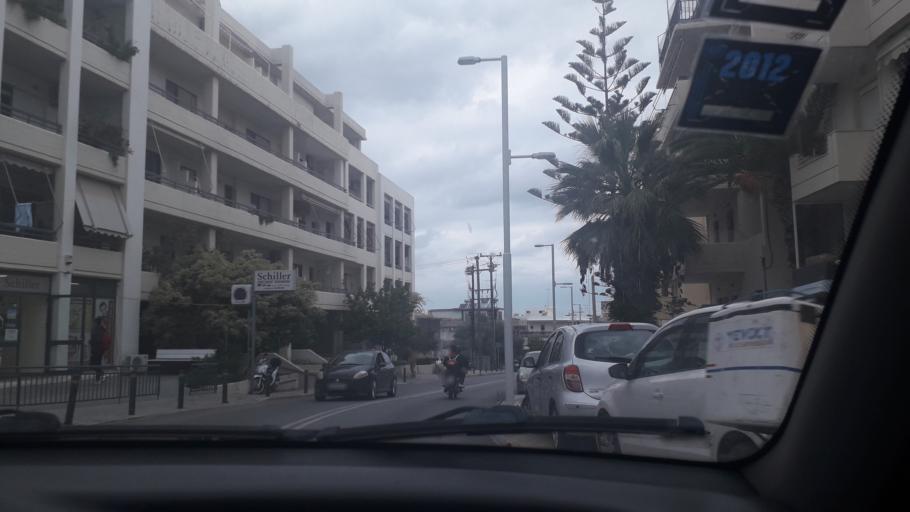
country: GR
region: Crete
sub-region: Nomos Rethymnis
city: Rethymno
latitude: 35.3616
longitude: 24.4731
